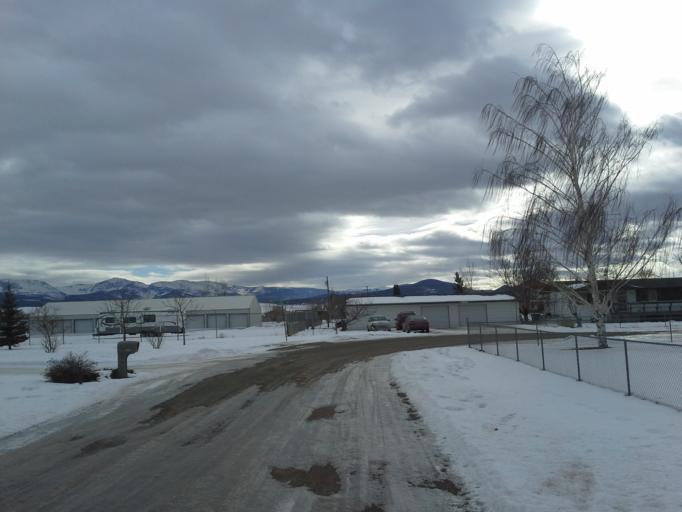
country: US
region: Montana
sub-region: Lewis and Clark County
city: East Helena
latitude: 46.5907
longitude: -111.9016
